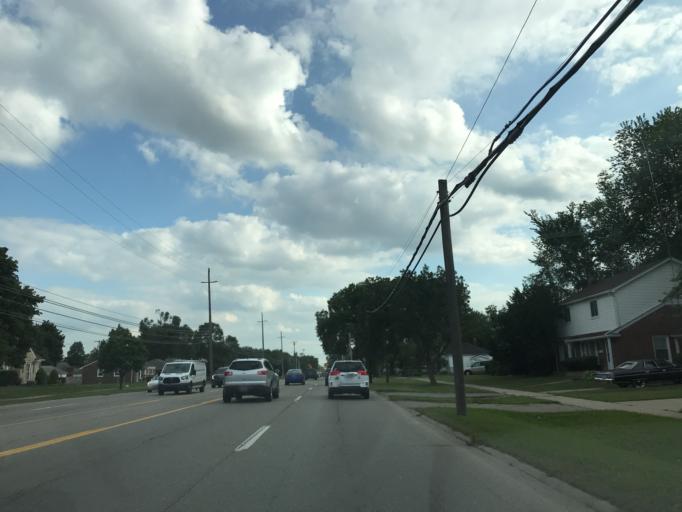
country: US
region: Michigan
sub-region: Wayne County
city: Redford
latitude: 42.3886
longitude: -83.2956
